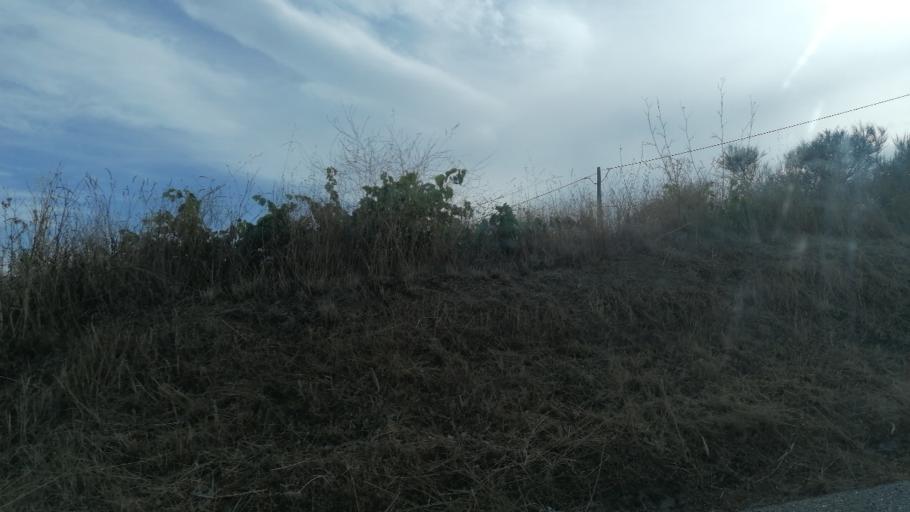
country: PT
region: Viseu
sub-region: Sao Joao da Pesqueira
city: Sao Joao da Pesqueira
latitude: 41.1039
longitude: -7.3854
